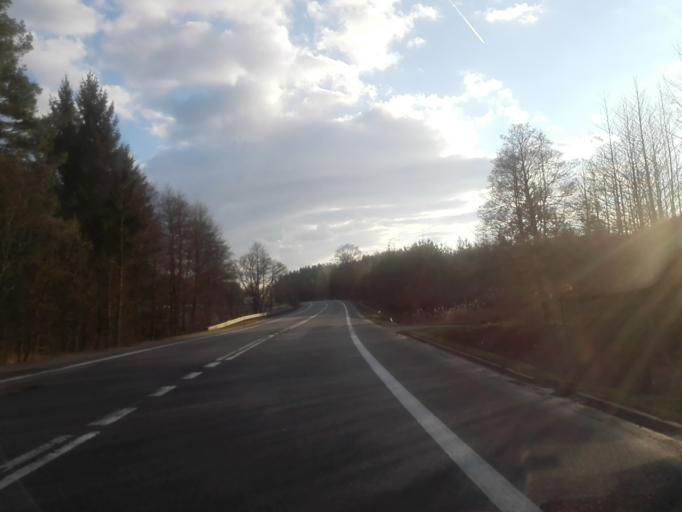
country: PL
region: Podlasie
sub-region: Suwalki
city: Suwalki
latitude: 54.1463
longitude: 22.9668
